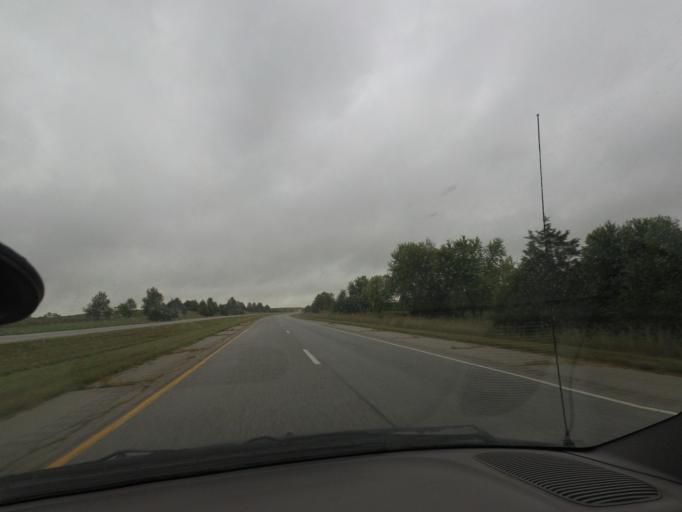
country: US
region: Illinois
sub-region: Pike County
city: Barry
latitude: 39.7374
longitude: -91.1445
